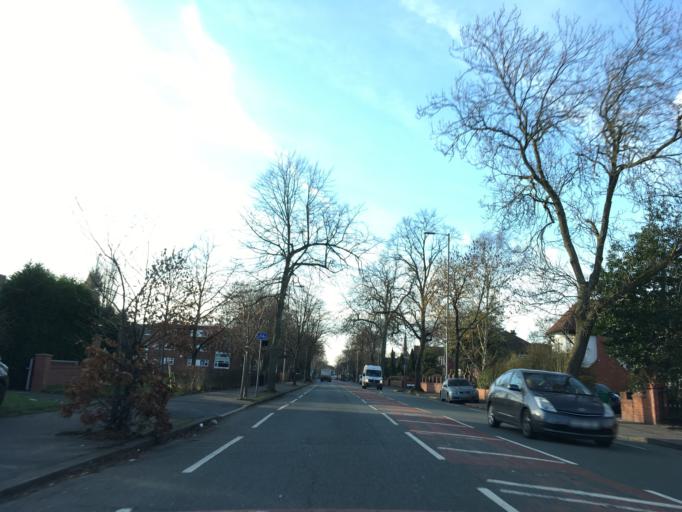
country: GB
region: England
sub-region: Manchester
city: Chorlton cum Hardy
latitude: 53.4431
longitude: -2.2644
